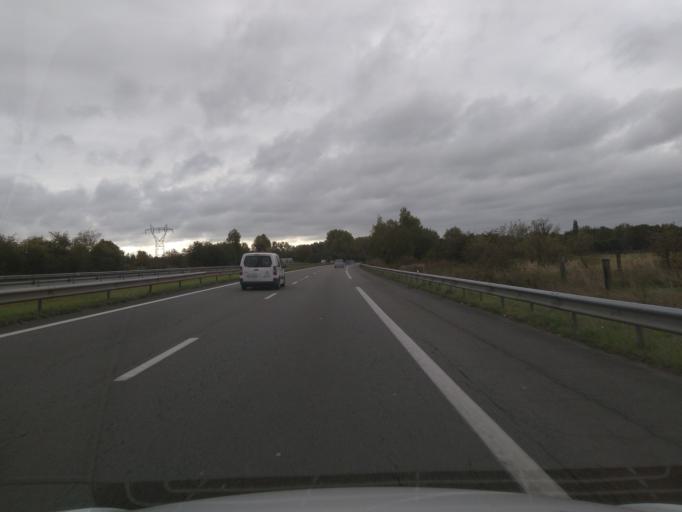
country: FR
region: Nord-Pas-de-Calais
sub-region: Departement du Nord
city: Genech
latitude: 50.5391
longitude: 3.1971
